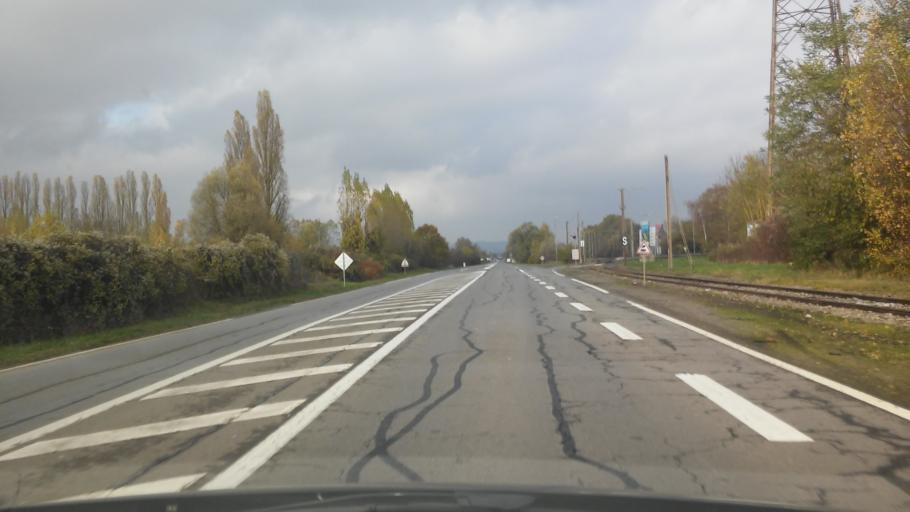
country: FR
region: Lorraine
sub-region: Departement de la Moselle
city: Uckange
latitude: 49.3118
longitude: 6.1584
